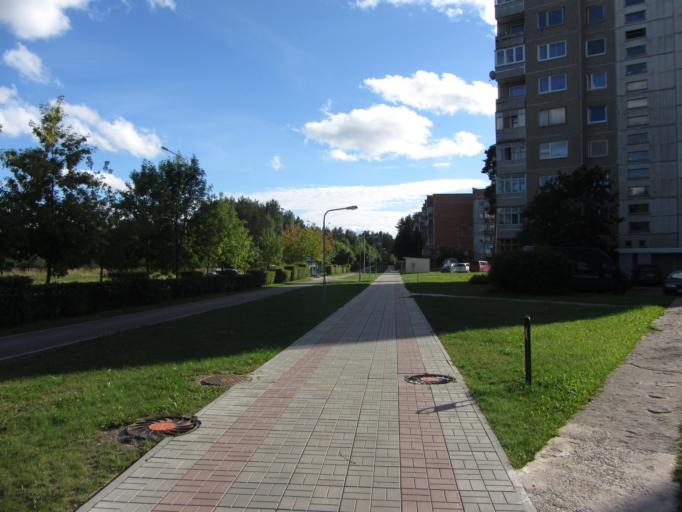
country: LT
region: Utenos apskritis
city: Visaginas
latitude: 55.5908
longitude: 26.4509
